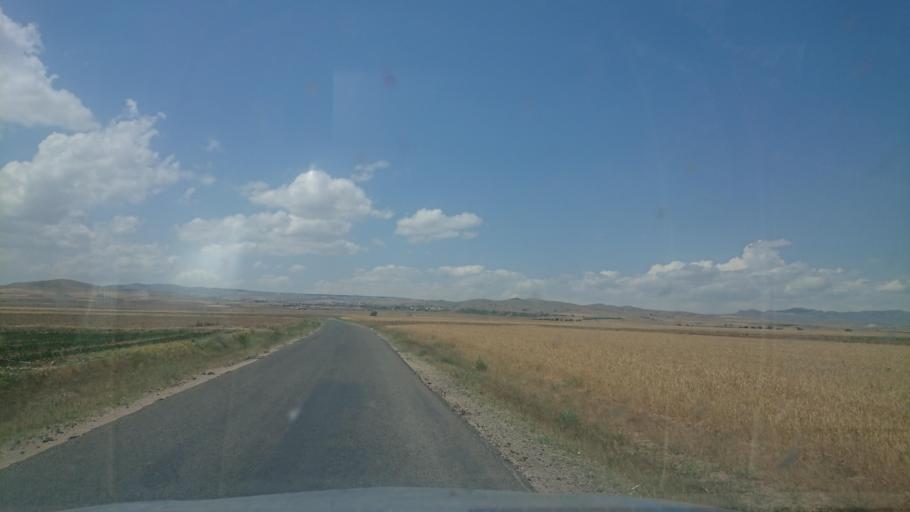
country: TR
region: Aksaray
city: Sariyahsi
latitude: 38.9994
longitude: 33.8849
